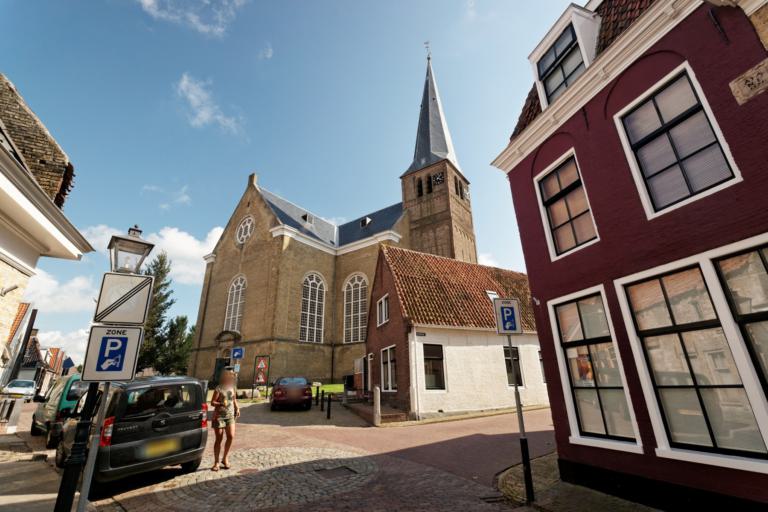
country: NL
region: Friesland
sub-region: Gemeente Harlingen
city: Harlingen
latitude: 53.1733
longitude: 5.4216
